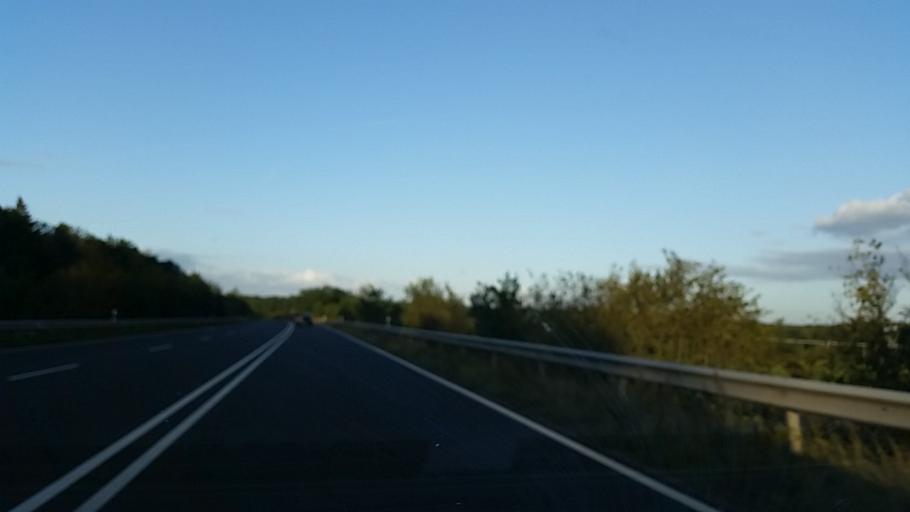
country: DE
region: Lower Saxony
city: Uelzen
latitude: 52.9335
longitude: 10.5566
